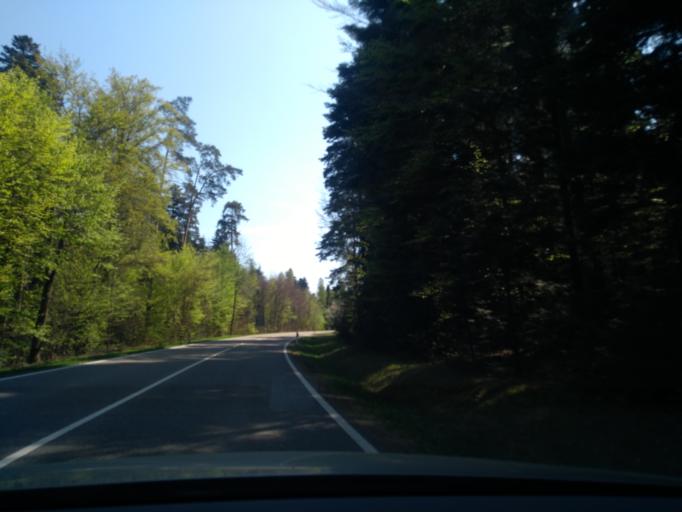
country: DE
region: Baden-Wuerttemberg
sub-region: Karlsruhe Region
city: Schomberg
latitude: 48.7889
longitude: 8.6644
